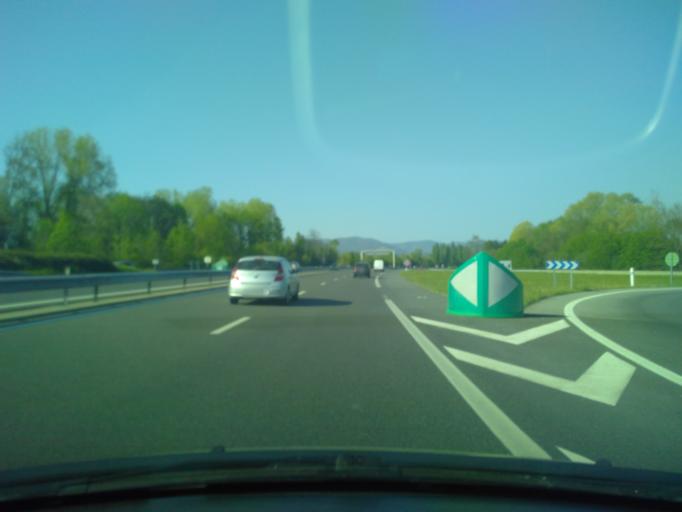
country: FR
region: Rhone-Alpes
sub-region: Departement de l'Isere
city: Saint-Quentin-sur-Isere
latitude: 45.2851
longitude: 5.5240
